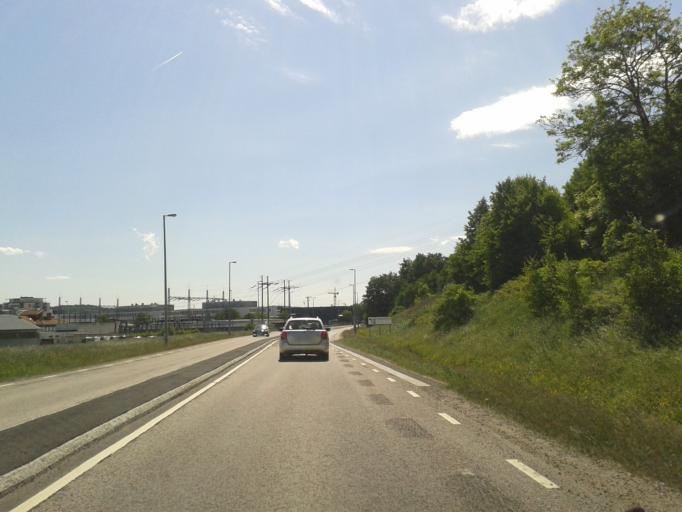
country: SE
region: Vaestra Goetaland
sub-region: Kungalvs Kommun
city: Kungalv
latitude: 57.8801
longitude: 11.9793
